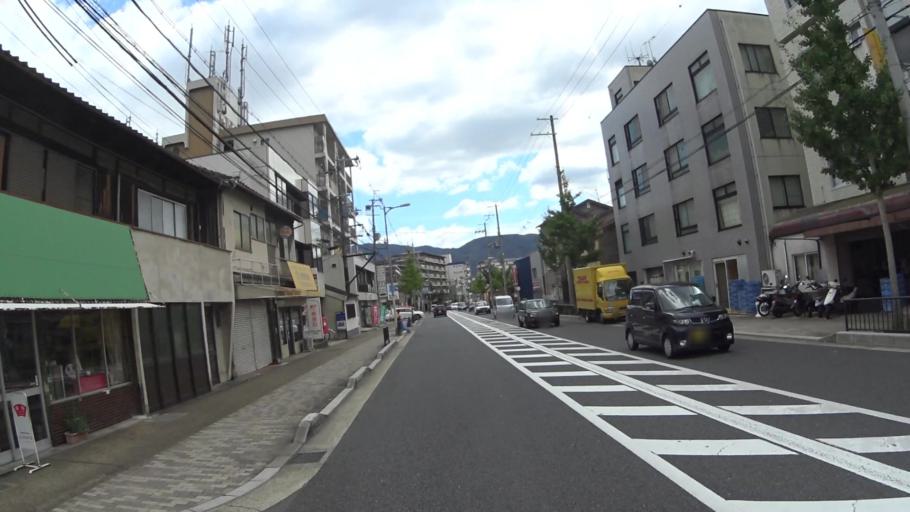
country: JP
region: Kyoto
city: Kyoto
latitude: 34.9956
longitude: 135.8027
